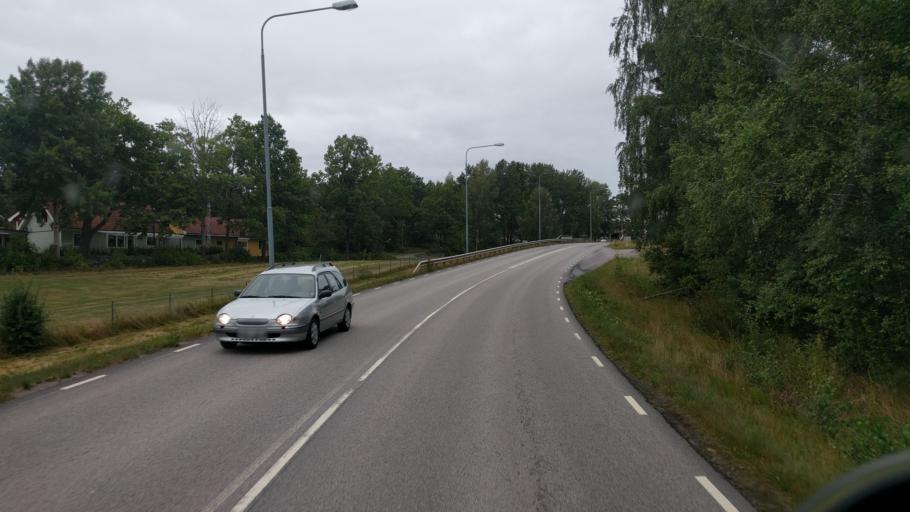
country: SE
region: Kalmar
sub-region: Vasterviks Kommun
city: Vaestervik
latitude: 57.7549
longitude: 16.6071
